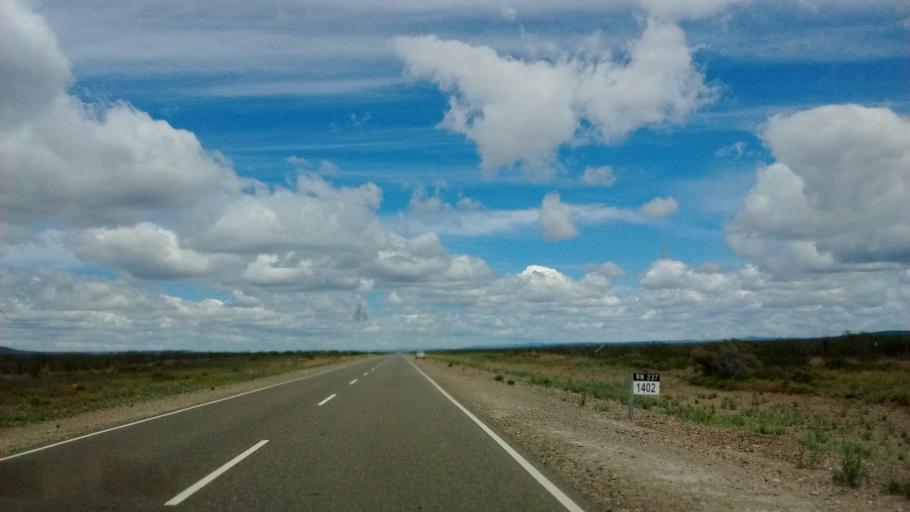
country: AR
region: Neuquen
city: Piedra del Aguila
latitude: -39.8077
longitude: -69.7089
